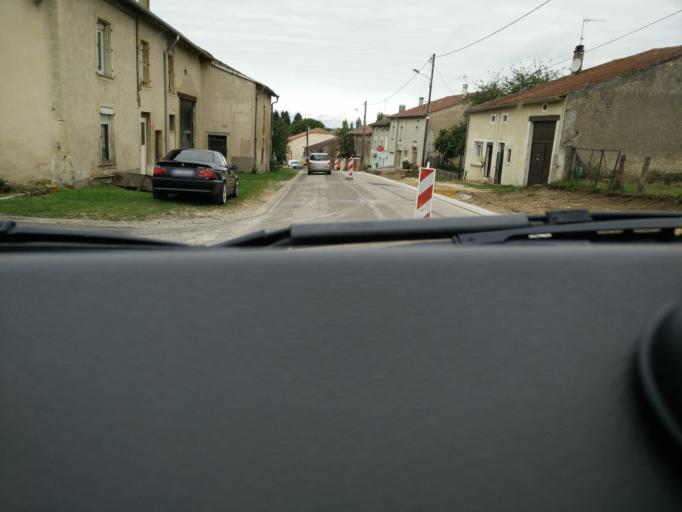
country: FR
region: Lorraine
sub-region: Departement de la Meuse
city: Vigneulles-les-Hattonchatel
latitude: 48.9617
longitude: 5.8281
